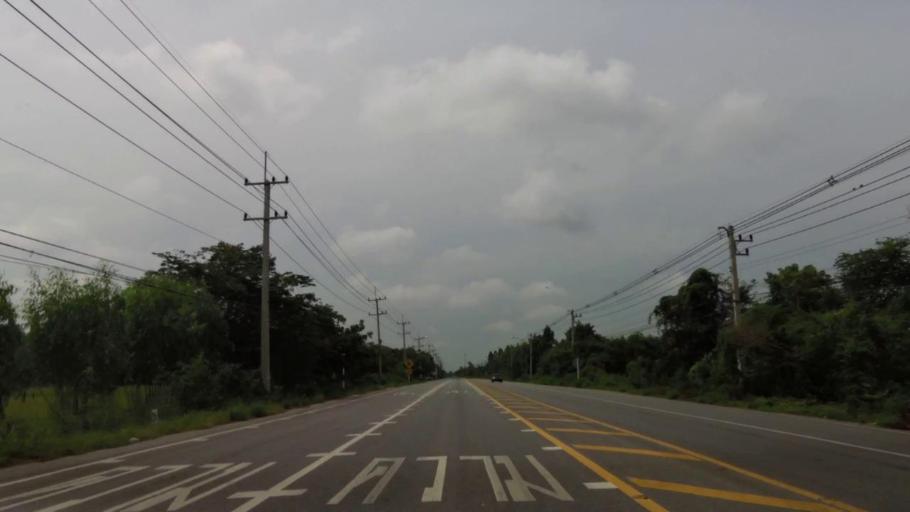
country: TH
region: Lop Buri
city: Ban Mi
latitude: 15.0654
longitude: 100.6255
